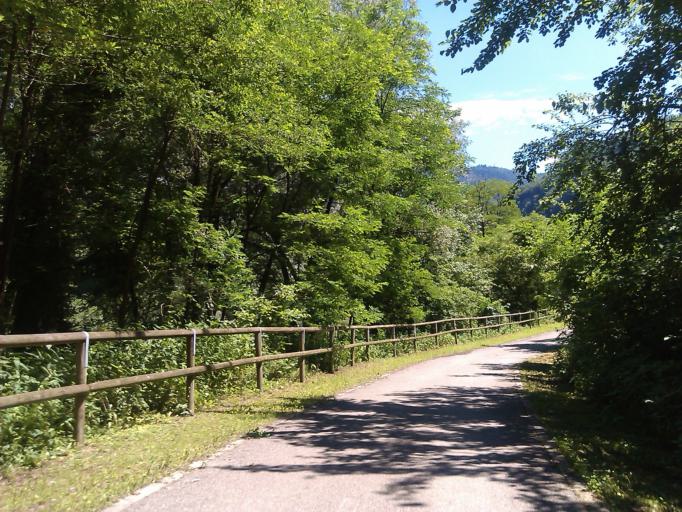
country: IT
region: Veneto
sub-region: Provincia di Vicenza
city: Enego
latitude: 45.9580
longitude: 11.7079
